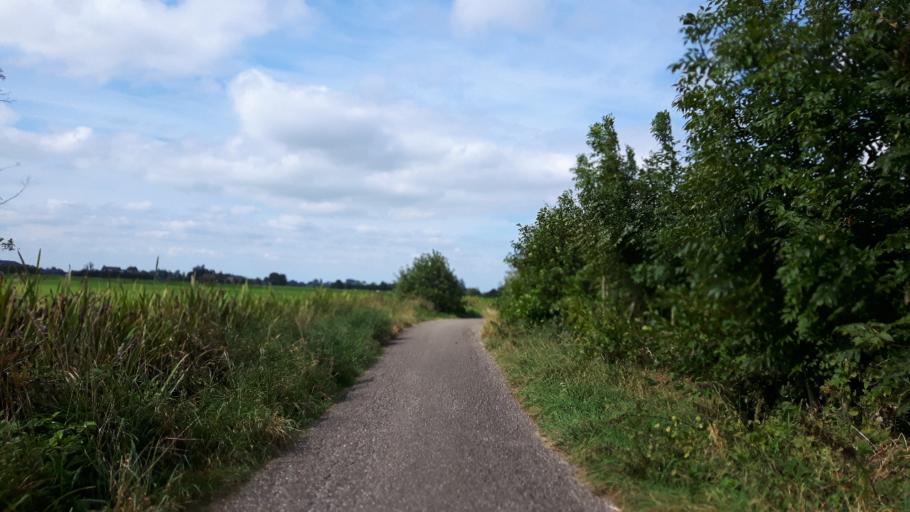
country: NL
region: Utrecht
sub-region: Gemeente Woerden
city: Woerden
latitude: 52.1189
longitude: 4.8408
